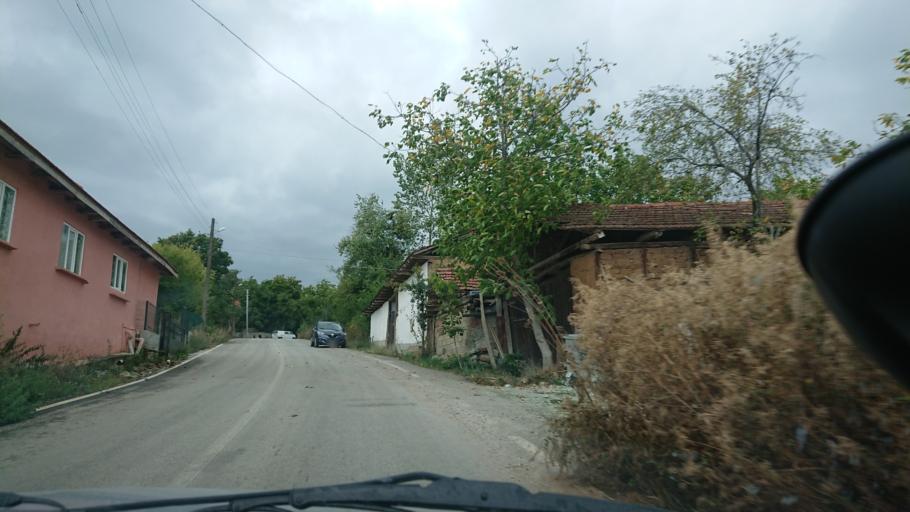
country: TR
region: Bilecik
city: Pazaryeri
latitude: 40.0113
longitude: 29.8003
